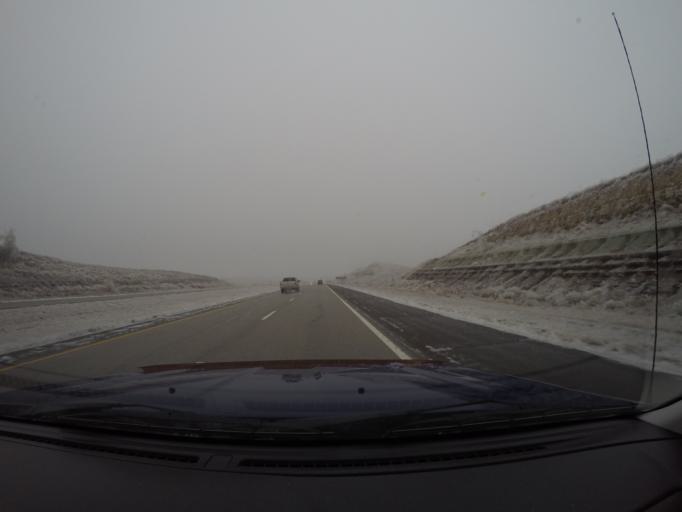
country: US
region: Kansas
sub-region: Riley County
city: Manhattan
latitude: 39.0730
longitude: -96.5382
